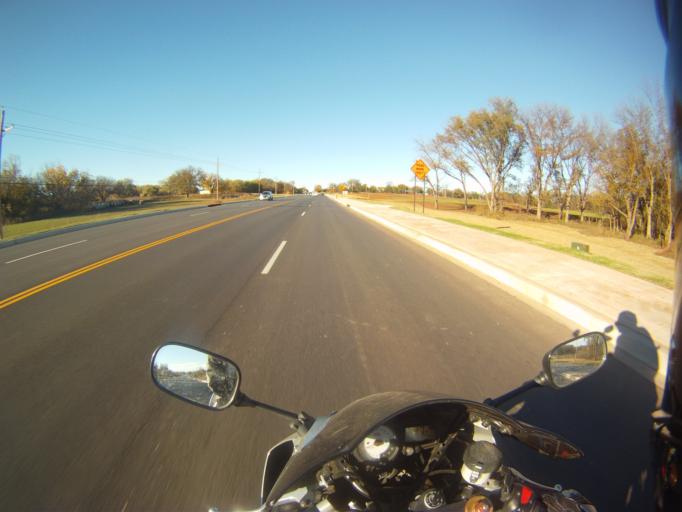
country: US
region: Oklahoma
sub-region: Payne County
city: Stillwater
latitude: 36.1270
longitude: -97.1230
